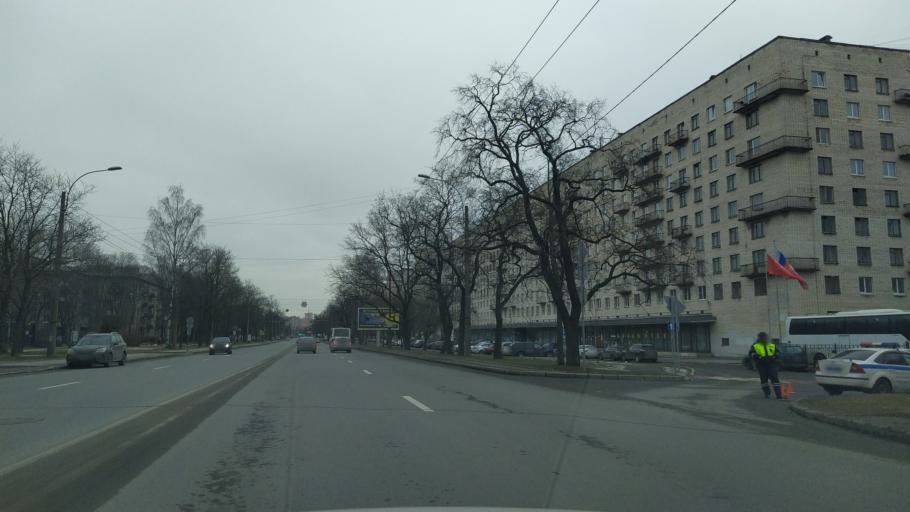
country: RU
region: St.-Petersburg
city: Sosnovka
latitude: 60.0056
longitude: 30.3557
